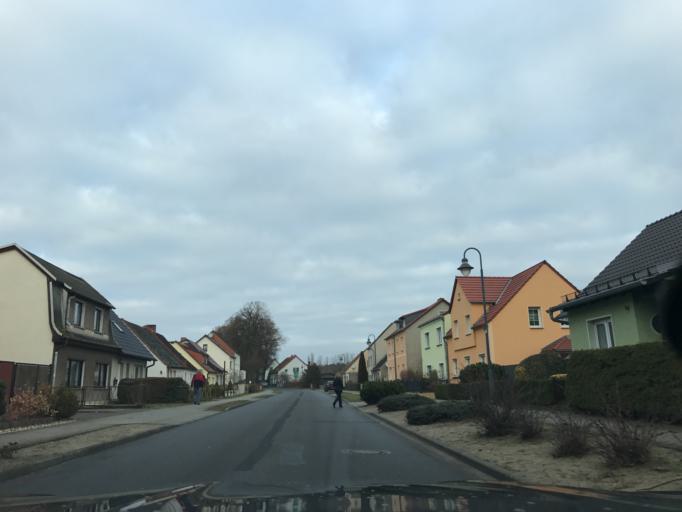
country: DE
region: Brandenburg
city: Gross Kreutz
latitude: 52.3210
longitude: 12.7359
